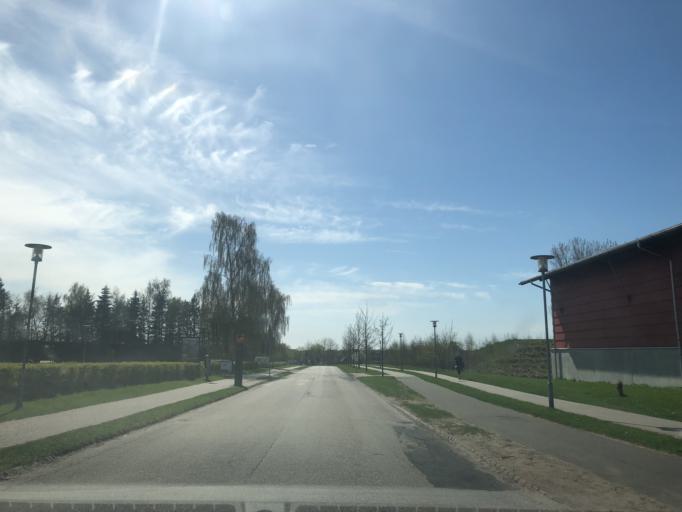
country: DK
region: Zealand
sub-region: Ringsted Kommune
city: Ringsted
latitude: 55.4279
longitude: 11.7830
